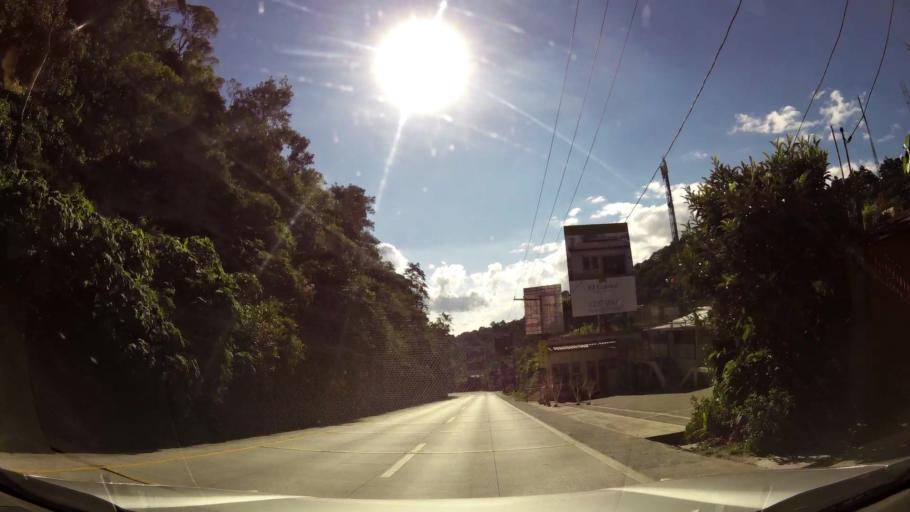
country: GT
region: Sacatepequez
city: Santa Lucia Milpas Altas
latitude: 14.5747
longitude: -90.6860
